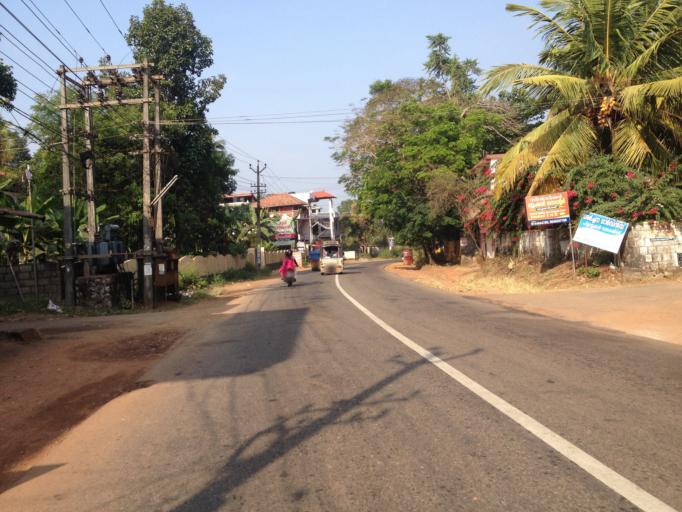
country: IN
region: Kerala
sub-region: Pattanamtitta
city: Adur
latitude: 9.1598
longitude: 76.7171
